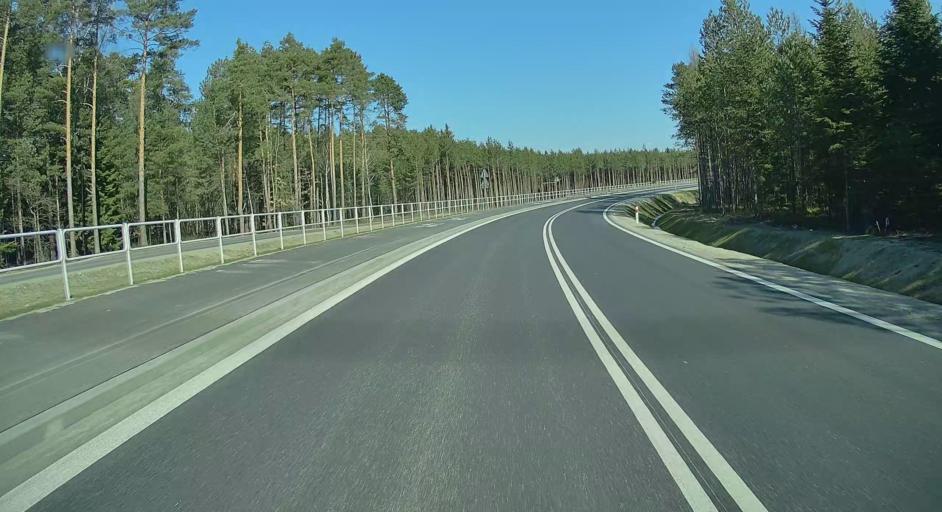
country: PL
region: Subcarpathian Voivodeship
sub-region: Powiat nizanski
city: Zarzecze
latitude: 50.5638
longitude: 22.2446
